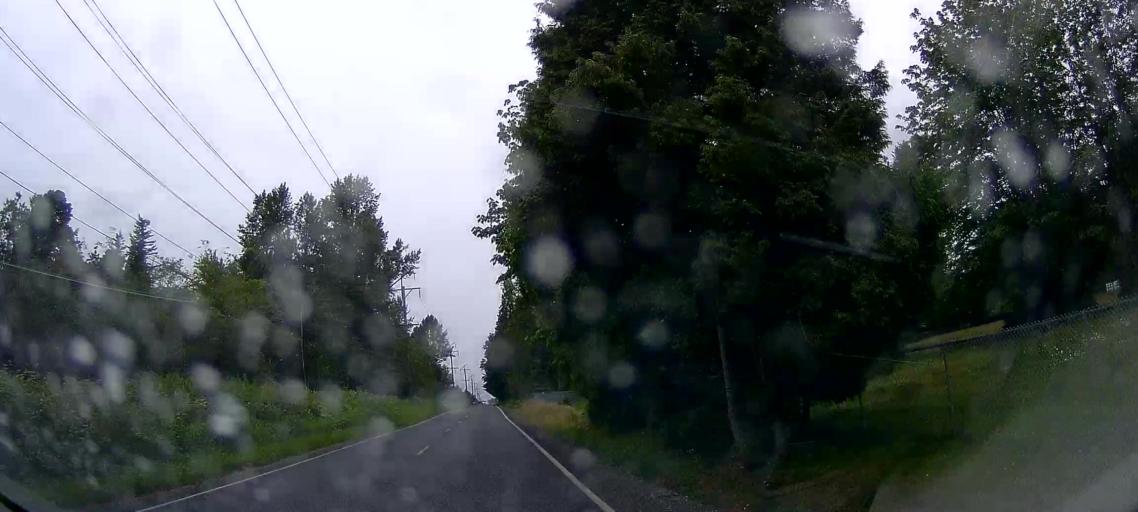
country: US
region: Washington
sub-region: Whatcom County
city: Birch Bay
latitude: 48.8815
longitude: -122.7043
